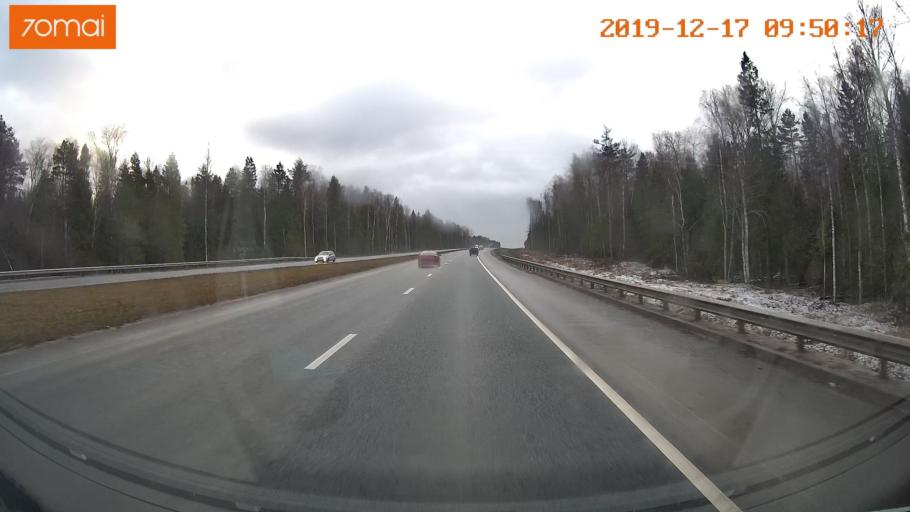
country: RU
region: Vladimir
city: Kommunar
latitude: 56.0599
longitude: 40.5073
